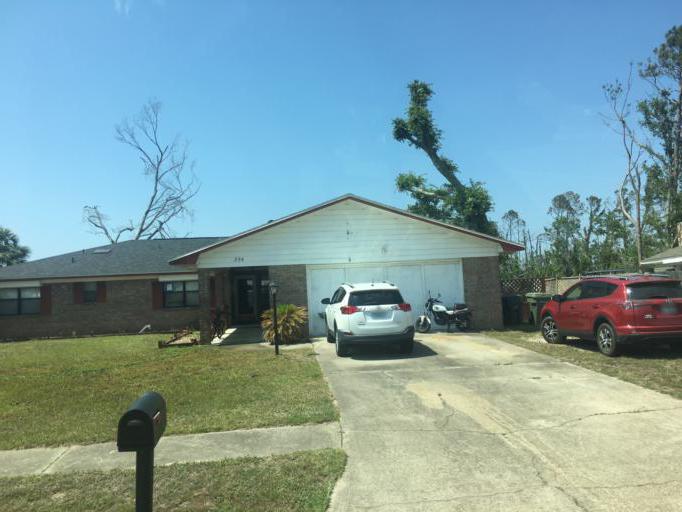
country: US
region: Florida
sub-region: Bay County
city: Lynn Haven
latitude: 30.2253
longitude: -85.6543
